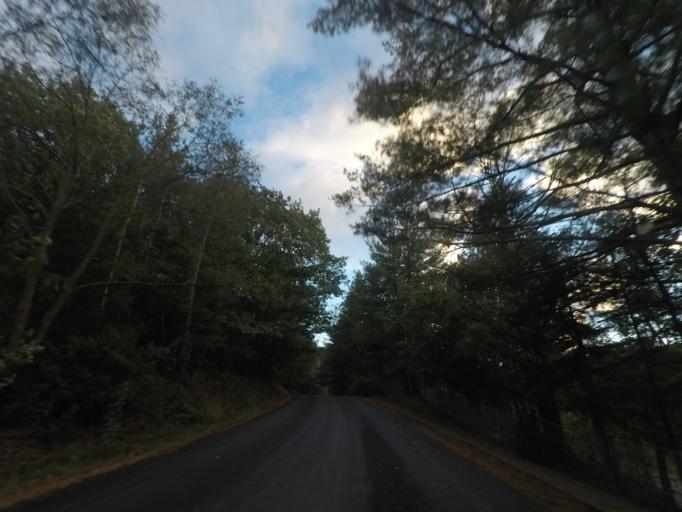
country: US
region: New York
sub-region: Rensselaer County
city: Nassau
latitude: 42.5339
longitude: -73.5782
